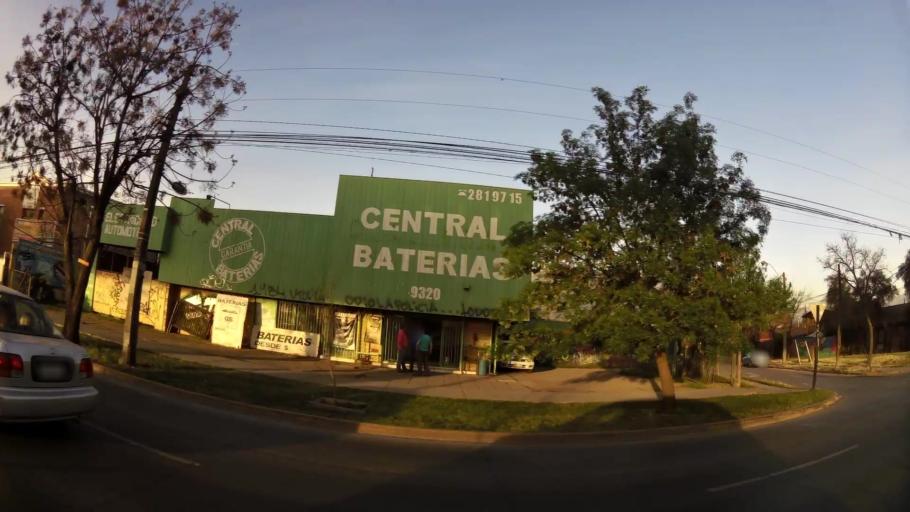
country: CL
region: Santiago Metropolitan
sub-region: Provincia de Santiago
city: La Pintana
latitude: -33.5416
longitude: -70.5900
